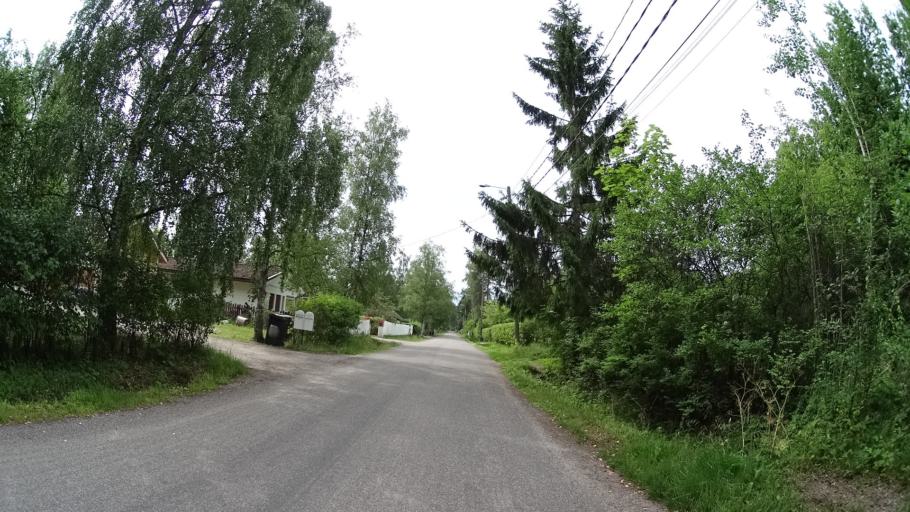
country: FI
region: Uusimaa
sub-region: Helsinki
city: Kilo
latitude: 60.2839
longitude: 24.7499
